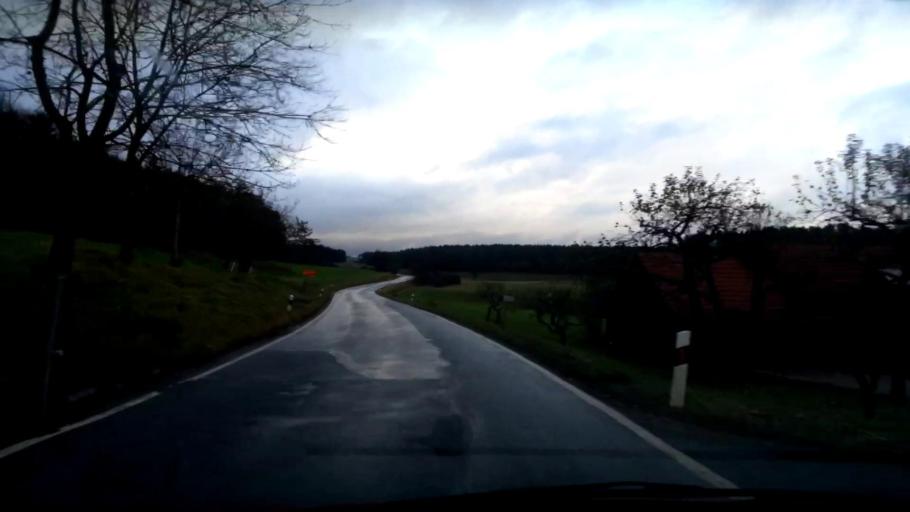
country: DE
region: Bavaria
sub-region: Upper Franconia
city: Poxdorf
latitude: 49.9216
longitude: 11.1274
